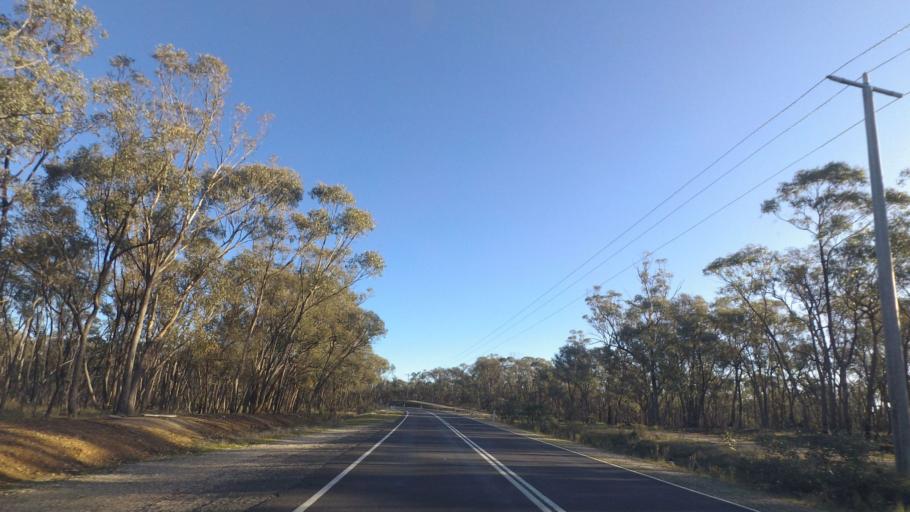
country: AU
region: Victoria
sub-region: Greater Bendigo
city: Kennington
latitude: -36.8753
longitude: 144.4947
